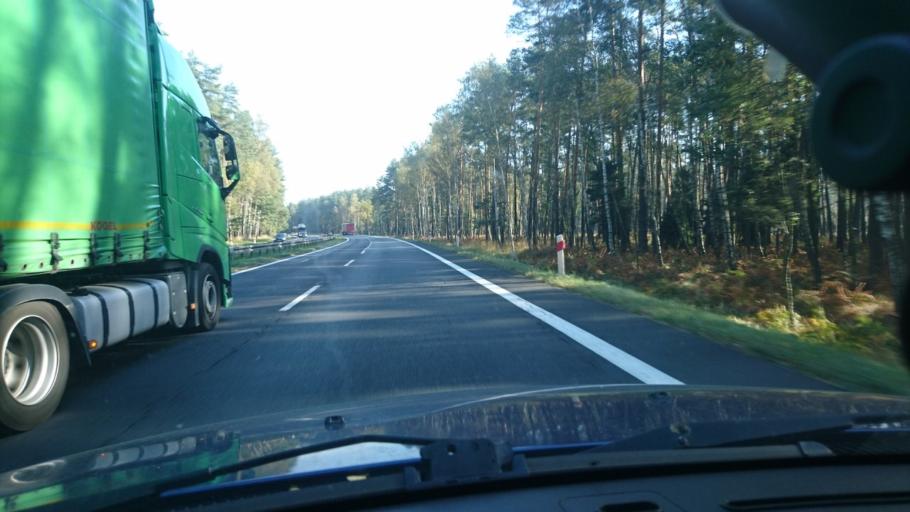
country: PL
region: Silesian Voivodeship
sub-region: Tychy
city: Cielmice
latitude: 50.0745
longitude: 18.9961
